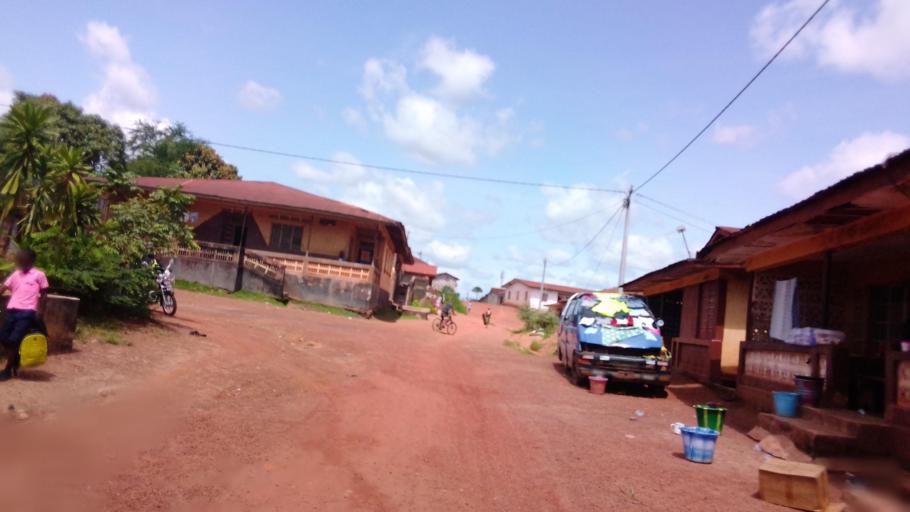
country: SL
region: Northern Province
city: Makeni
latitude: 8.8858
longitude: -12.0358
